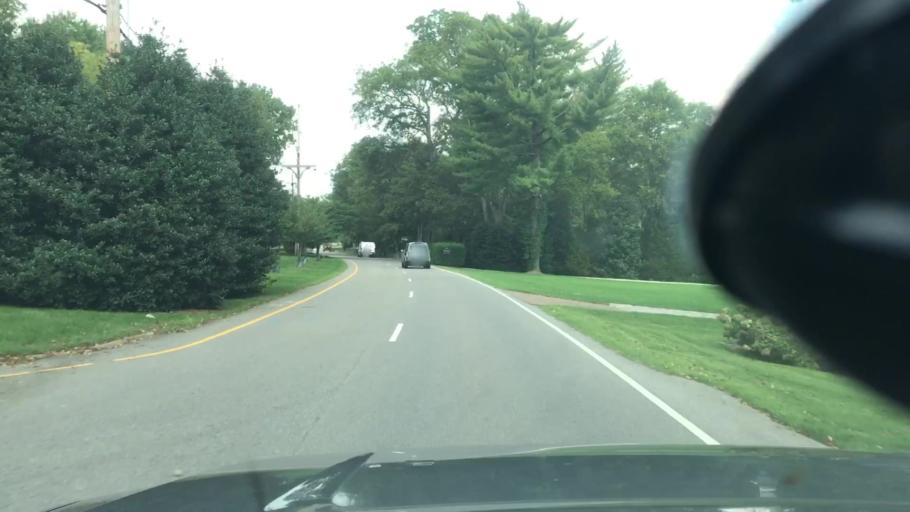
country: US
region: Tennessee
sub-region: Davidson County
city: Belle Meade
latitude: 36.1130
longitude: -86.8546
